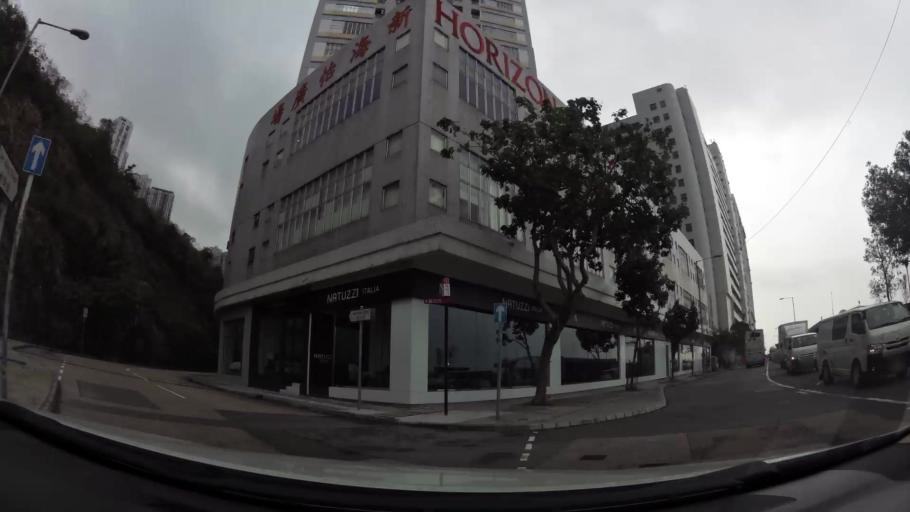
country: HK
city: Sok Kwu Wan
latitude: 22.2392
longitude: 114.1519
